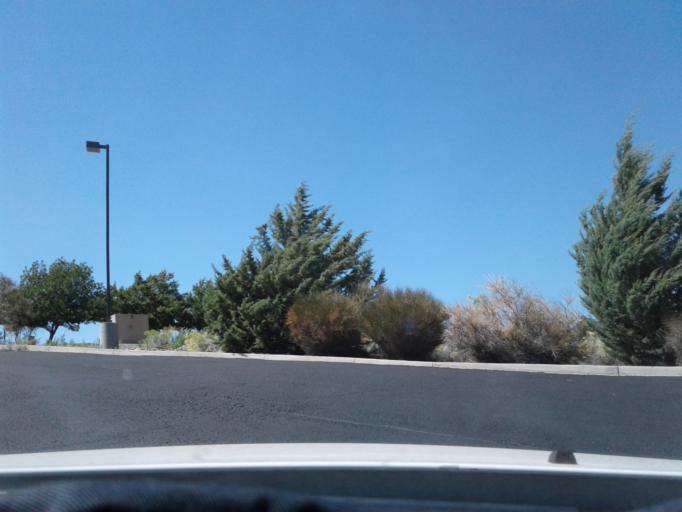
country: US
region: Arizona
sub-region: Yavapai County
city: Prescott
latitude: 34.5743
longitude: -112.4460
